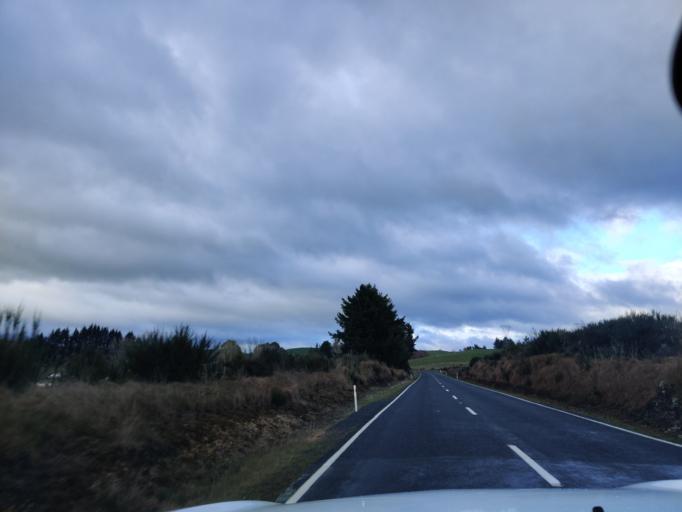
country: NZ
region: Waikato
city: Turangi
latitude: -38.8385
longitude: 175.6887
